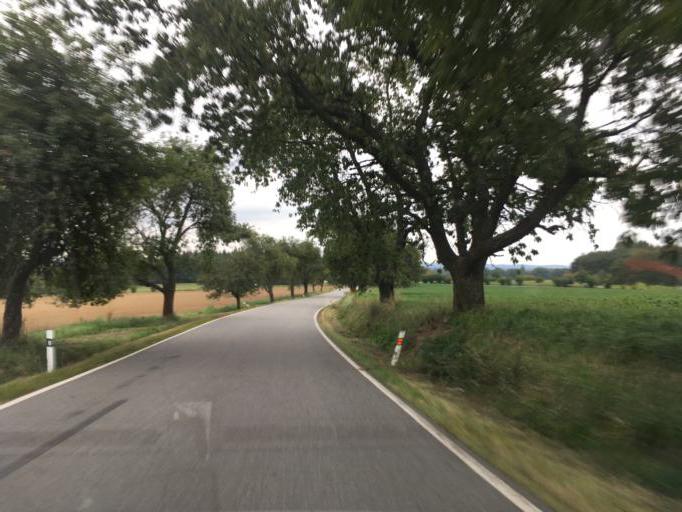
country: CZ
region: Vysocina
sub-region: Okres Jihlava
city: Telc
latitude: 49.2161
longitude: 15.4264
